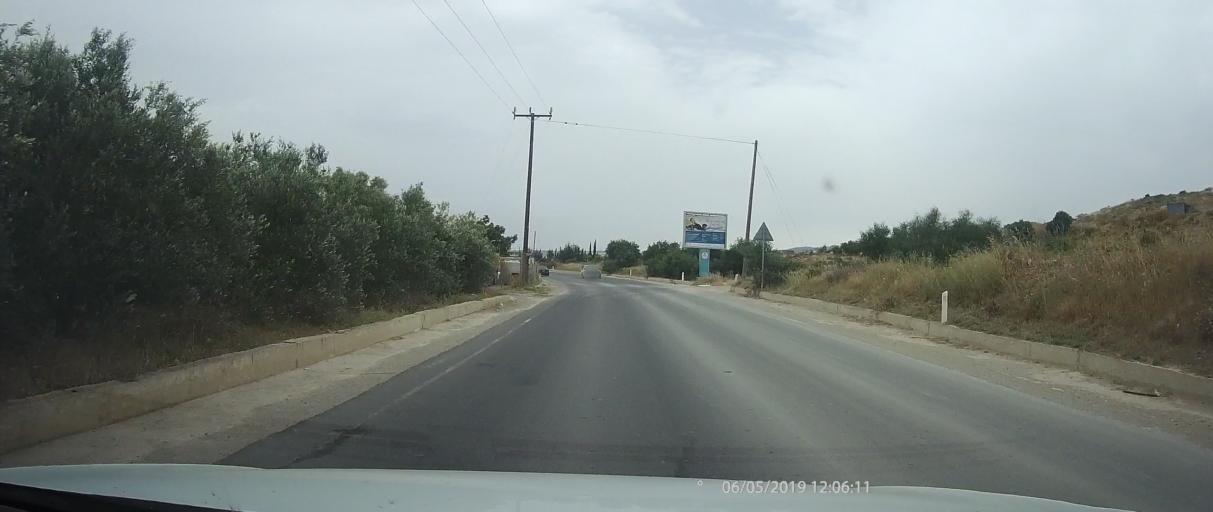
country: CY
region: Pafos
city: Empa
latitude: 34.8149
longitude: 32.4286
